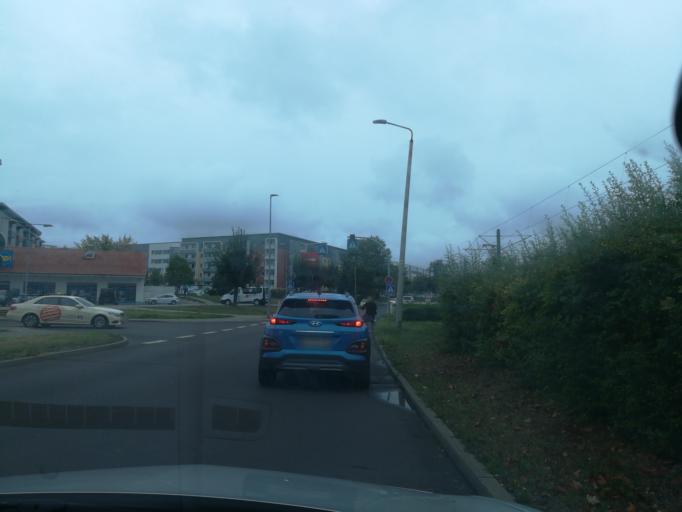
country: DE
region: Saxony-Anhalt
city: Diesdorf
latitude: 52.1506
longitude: 11.5862
